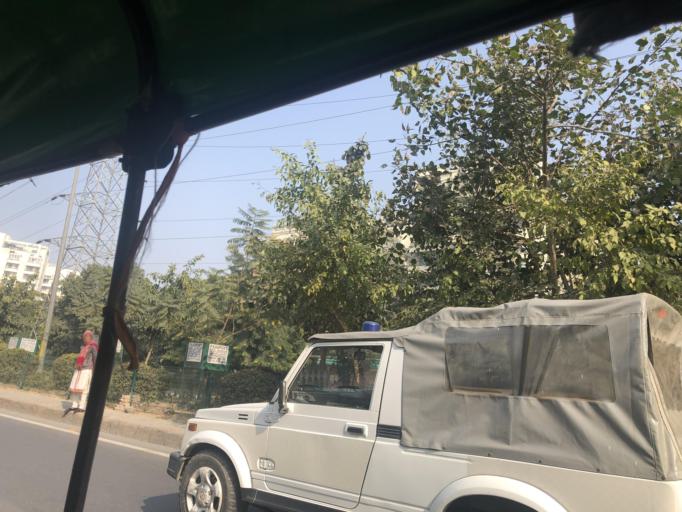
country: IN
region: Haryana
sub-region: Gurgaon
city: Gurgaon
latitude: 28.4483
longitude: 77.0784
